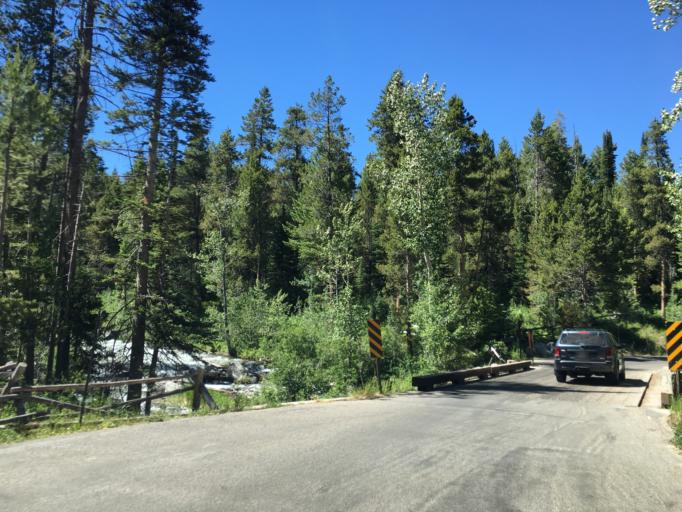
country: US
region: Wyoming
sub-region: Teton County
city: Moose Wilson Road
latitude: 43.6258
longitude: -110.7840
